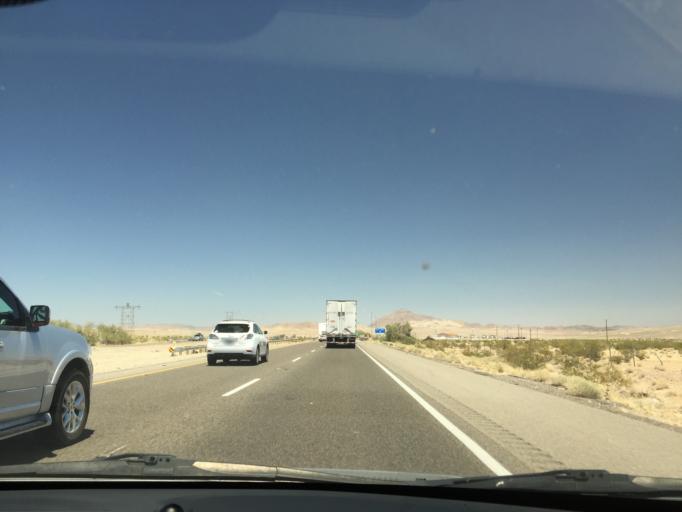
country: US
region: California
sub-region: San Bernardino County
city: Fort Irwin
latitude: 35.0303
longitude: -116.4767
